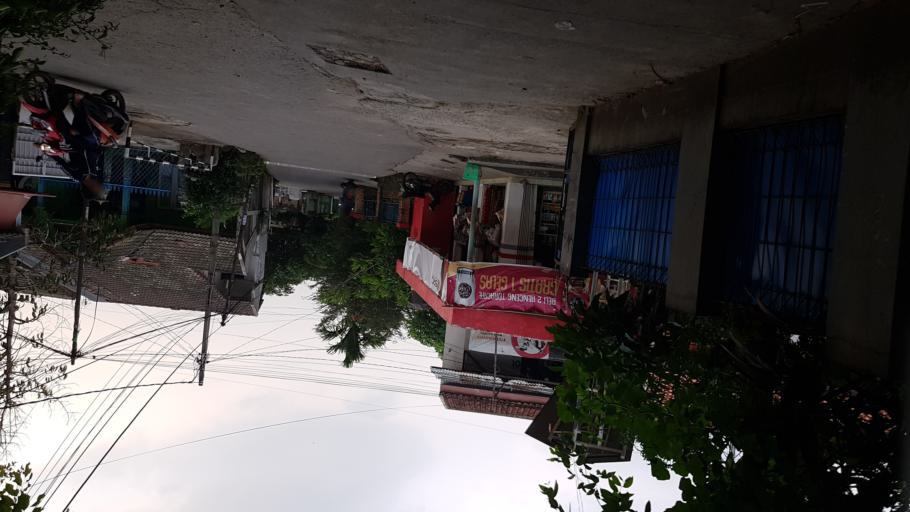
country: ID
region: West Java
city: Depok
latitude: -6.3812
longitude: 106.8051
